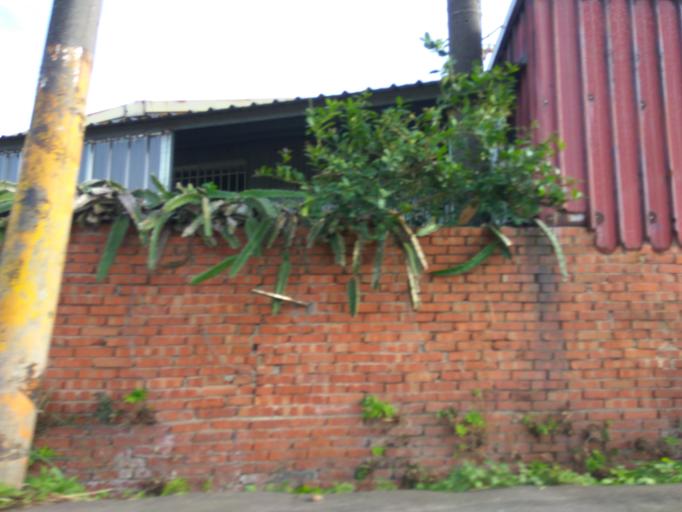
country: TW
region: Taiwan
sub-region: Hsinchu
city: Zhubei
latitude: 24.9415
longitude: 120.9922
